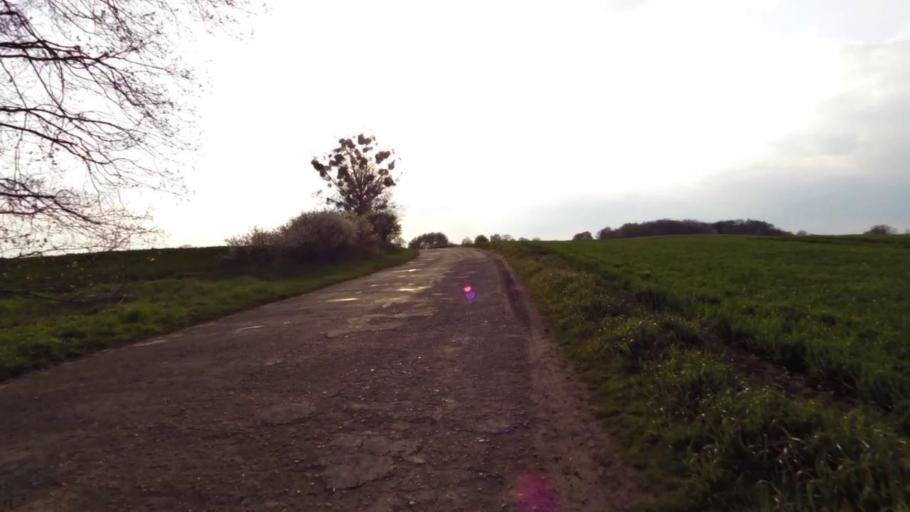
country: PL
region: West Pomeranian Voivodeship
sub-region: Powiat mysliborski
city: Mysliborz
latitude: 52.9004
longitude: 14.7650
